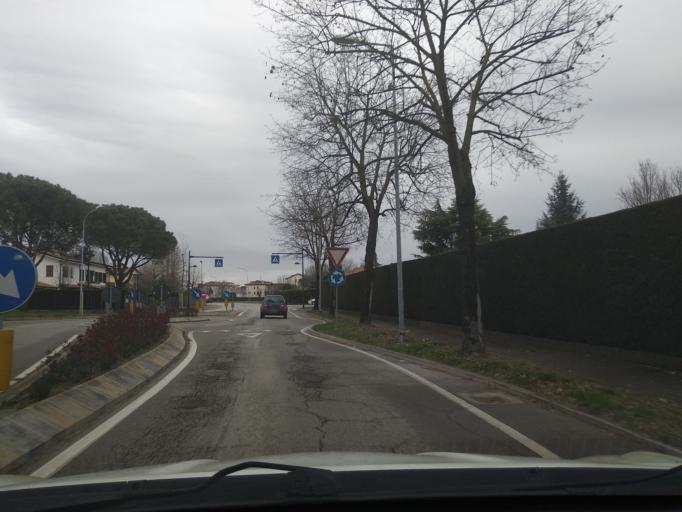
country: IT
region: Veneto
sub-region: Provincia di Padova
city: Selvazzano Dentro
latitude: 45.3900
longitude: 11.7849
